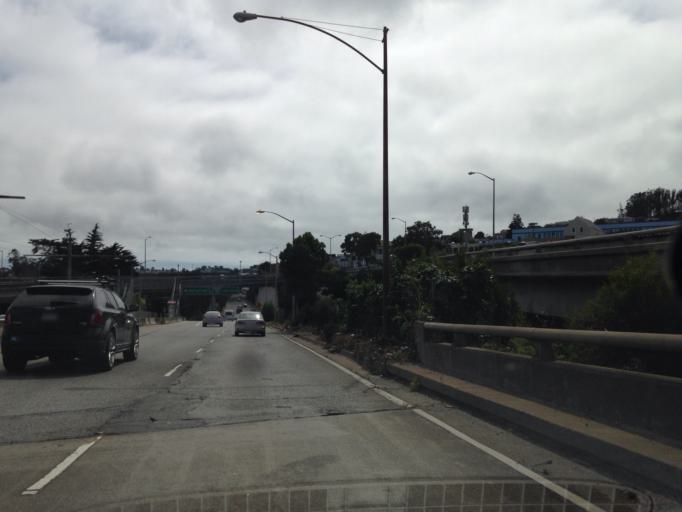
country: US
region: California
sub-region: San Mateo County
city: Daly City
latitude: 37.7331
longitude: -122.4326
